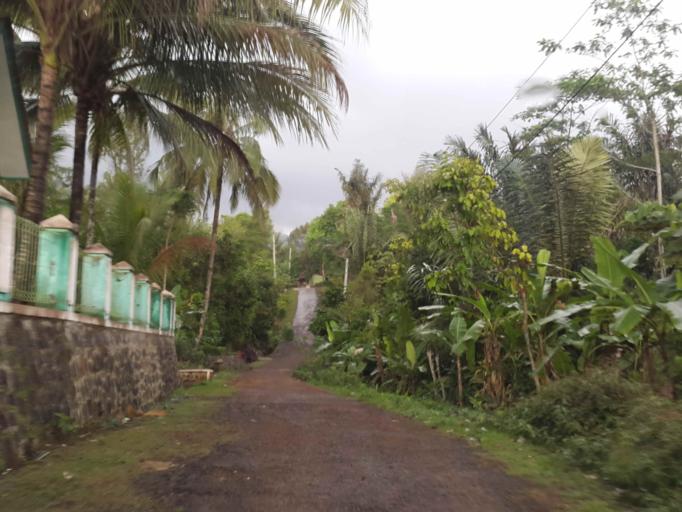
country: ID
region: Central Java
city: Limbangan
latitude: -7.2811
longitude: 108.7039
